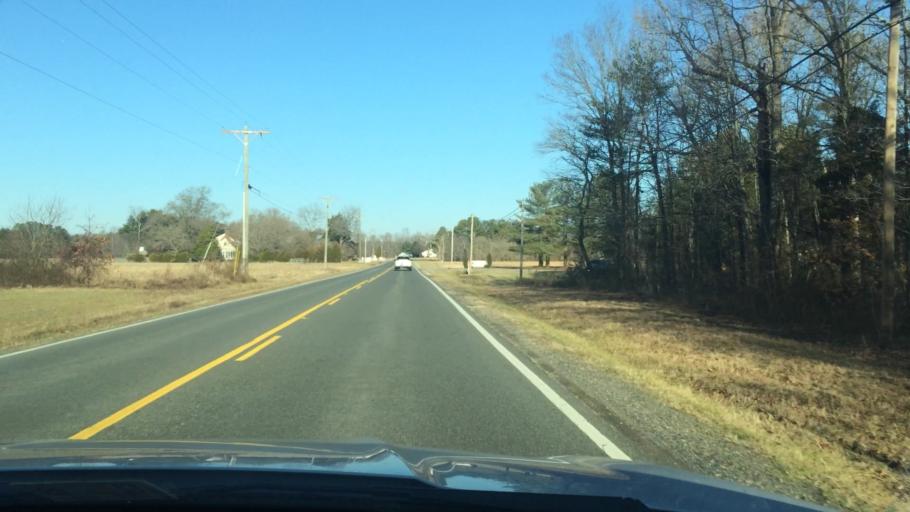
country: US
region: Virginia
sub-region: Lancaster County
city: Lancaster
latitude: 37.7568
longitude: -76.4177
